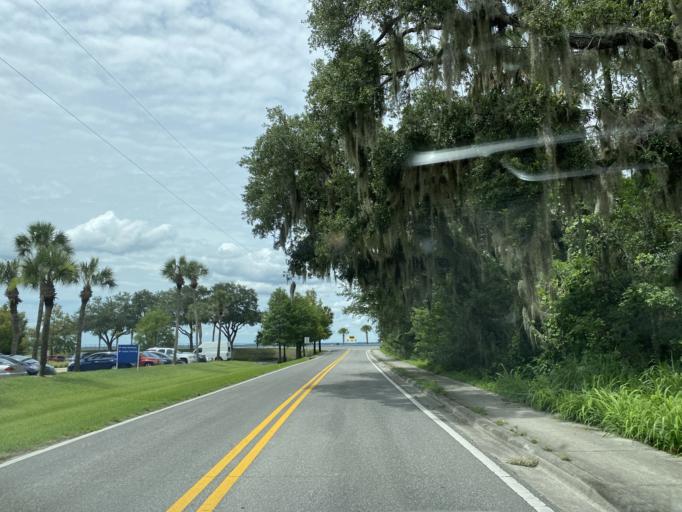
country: US
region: Florida
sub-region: Seminole County
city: Sanford
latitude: 28.8151
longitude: -81.2827
